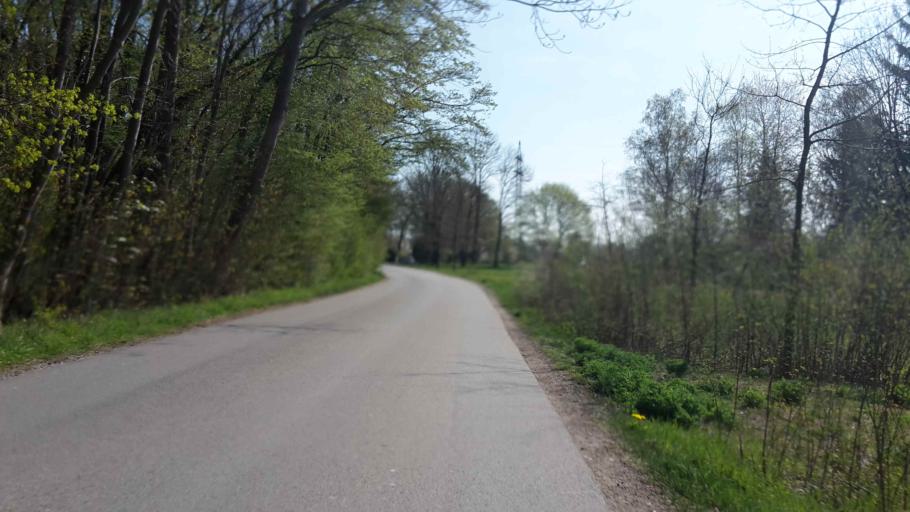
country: DE
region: Bavaria
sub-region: Upper Bavaria
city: Karlsfeld
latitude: 48.1968
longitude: 11.4466
